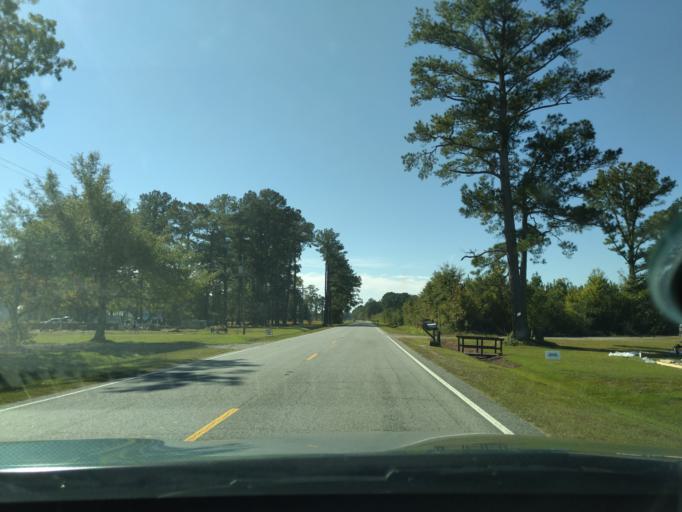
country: US
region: North Carolina
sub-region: Washington County
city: Plymouth
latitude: 35.6706
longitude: -76.7876
